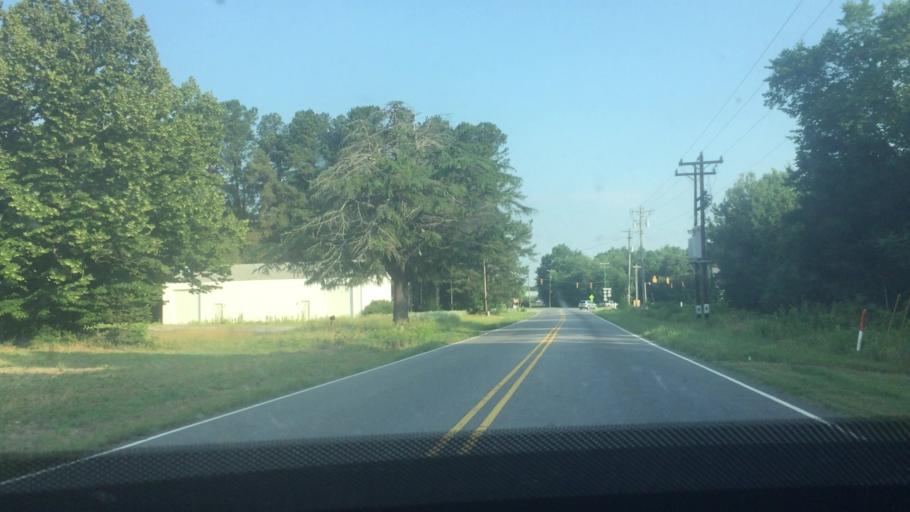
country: US
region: North Carolina
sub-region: Iredell County
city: Mooresville
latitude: 35.5967
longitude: -80.7631
